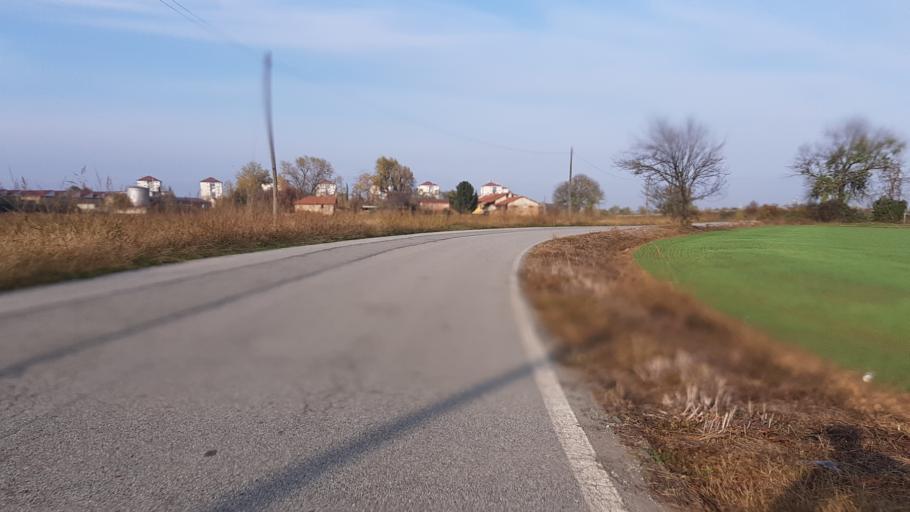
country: IT
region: Piedmont
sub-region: Provincia di Torino
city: Settimo Torinese
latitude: 45.1269
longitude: 7.7256
